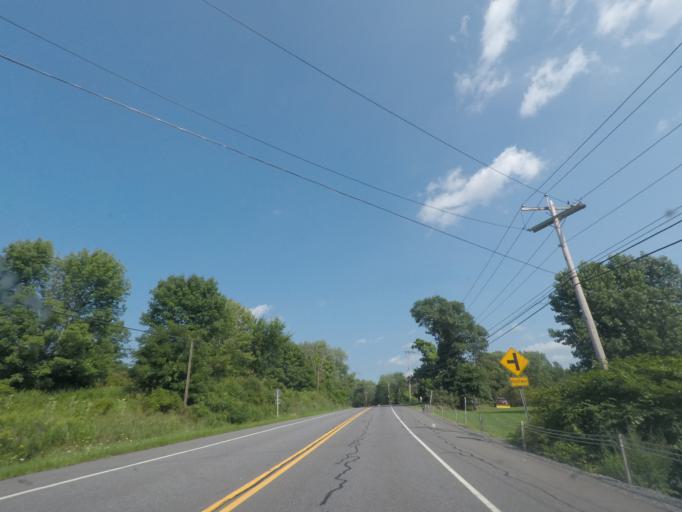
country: US
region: New York
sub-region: Rensselaer County
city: Nassau
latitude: 42.5287
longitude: -73.6518
